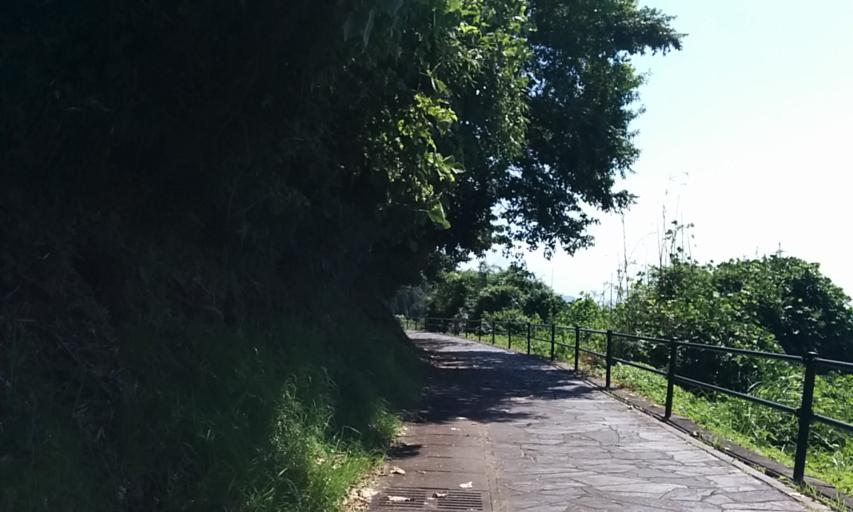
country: JP
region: Kagoshima
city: Kajiki
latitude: 31.7536
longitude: 130.6666
